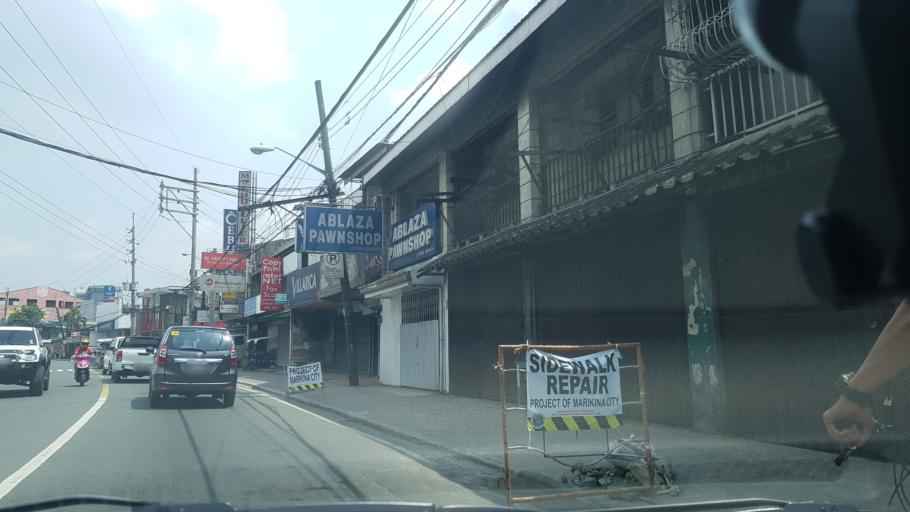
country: PH
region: Metro Manila
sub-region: Marikina
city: Calumpang
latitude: 14.6501
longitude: 121.1025
